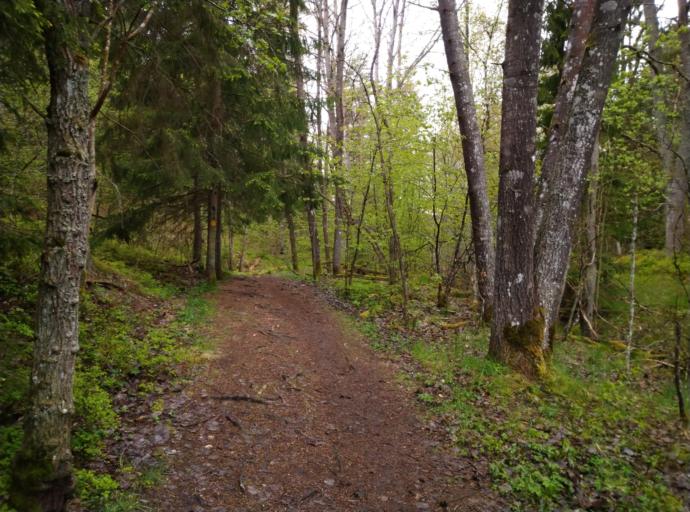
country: SE
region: Stockholm
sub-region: Nacka Kommun
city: Saltsjobaden
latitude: 59.2961
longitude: 18.2837
